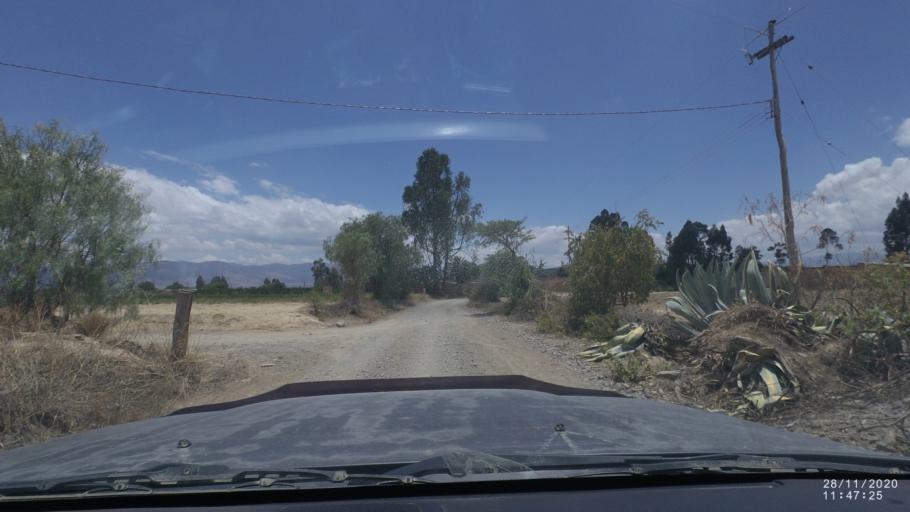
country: BO
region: Cochabamba
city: Tarata
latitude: -17.6448
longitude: -66.0362
